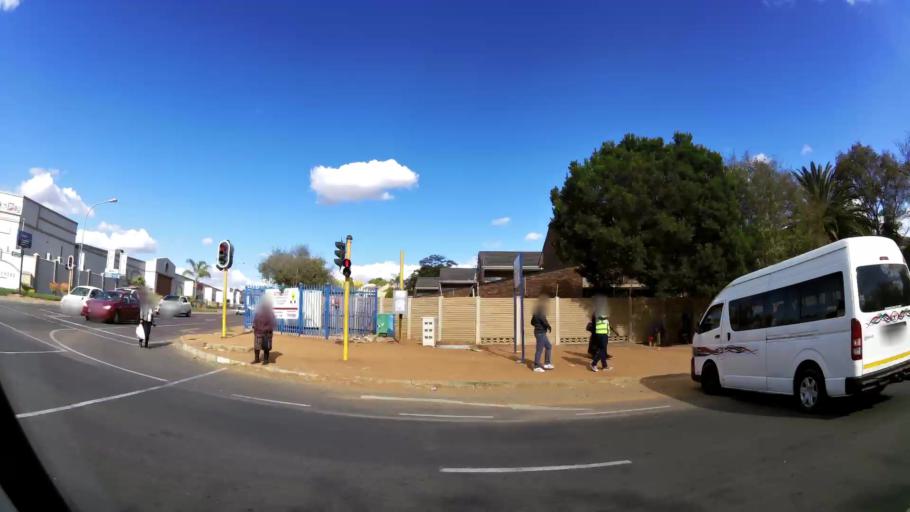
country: ZA
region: Limpopo
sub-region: Capricorn District Municipality
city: Polokwane
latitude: -23.8929
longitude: 29.4717
